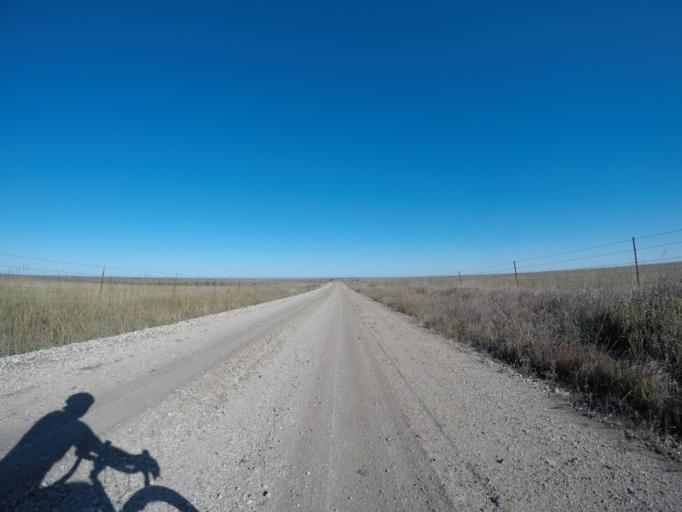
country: US
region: Kansas
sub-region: Wabaunsee County
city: Alma
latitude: 38.8826
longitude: -96.4096
